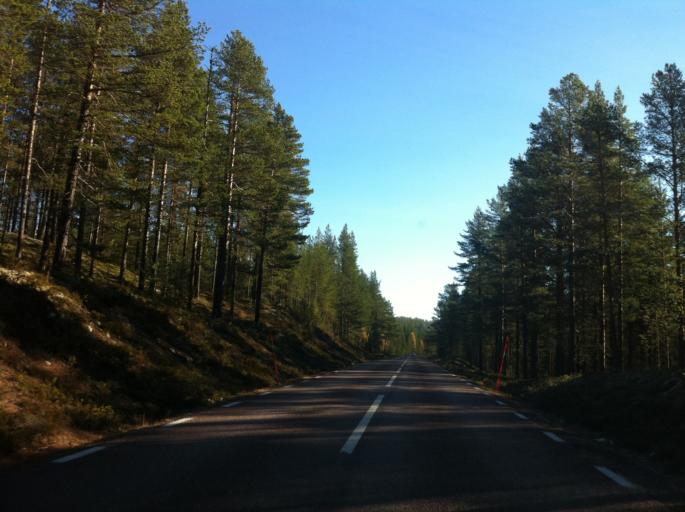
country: NO
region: Hedmark
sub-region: Trysil
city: Innbygda
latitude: 61.8430
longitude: 12.7920
